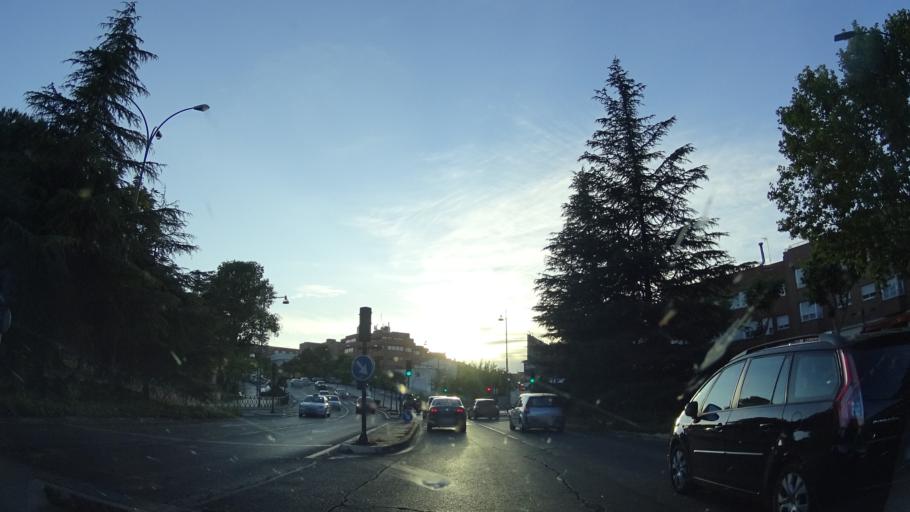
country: ES
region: Madrid
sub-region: Provincia de Madrid
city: Alcobendas
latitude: 40.5479
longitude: -3.6364
